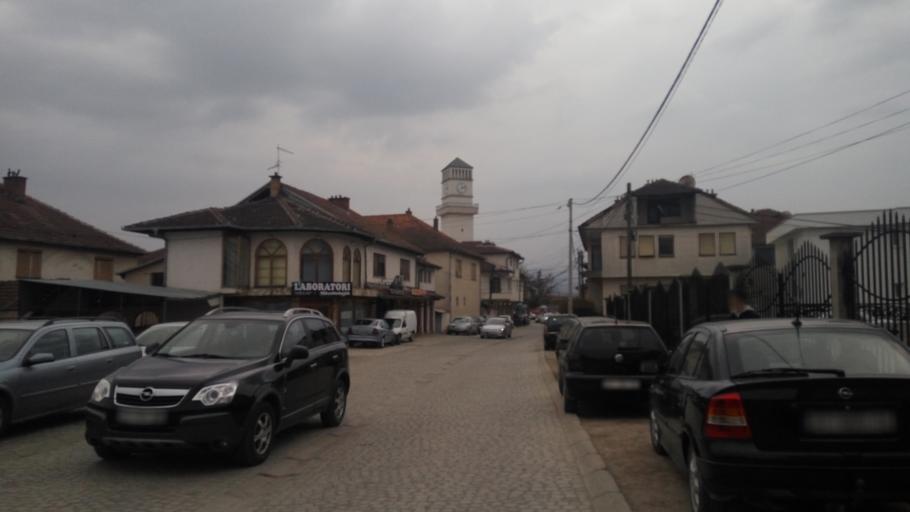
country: XK
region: Gjakova
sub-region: Komuna e Gjakoves
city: Gjakove
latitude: 42.3816
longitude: 20.4278
